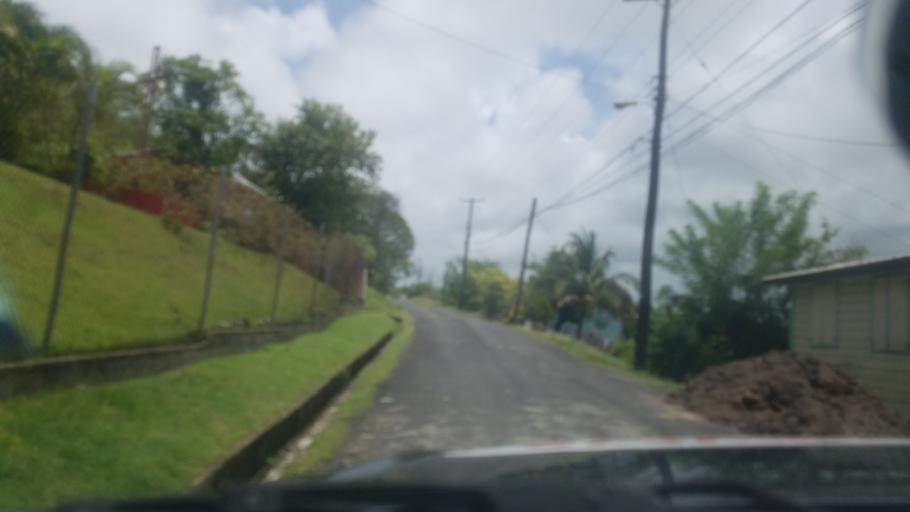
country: LC
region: Laborie Quarter
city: Laborie
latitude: 13.7415
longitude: -60.9596
